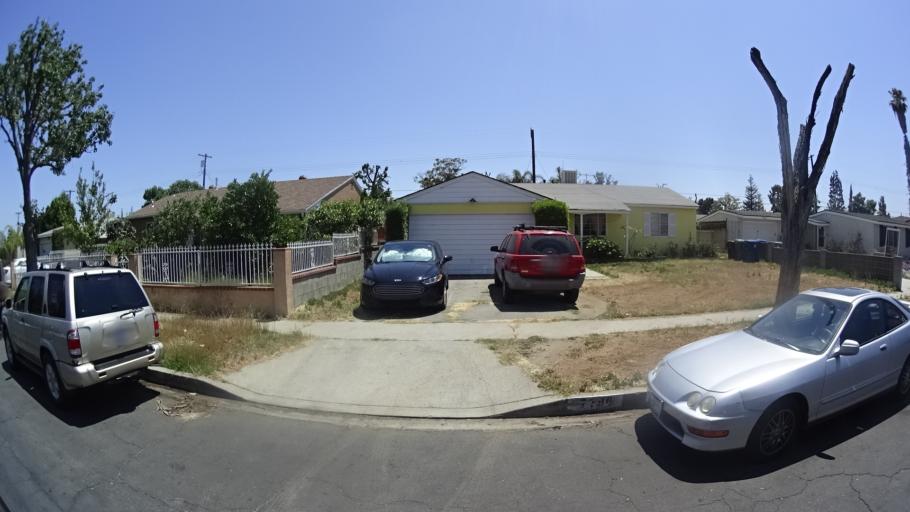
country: US
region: California
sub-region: Los Angeles County
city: Van Nuys
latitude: 34.2119
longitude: -118.4333
